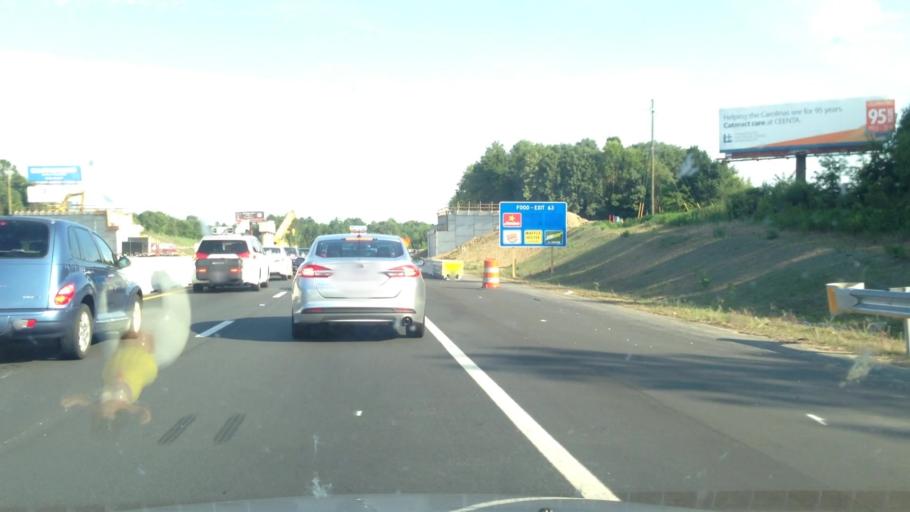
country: US
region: North Carolina
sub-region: Rowan County
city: Landis
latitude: 35.5104
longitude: -80.5657
